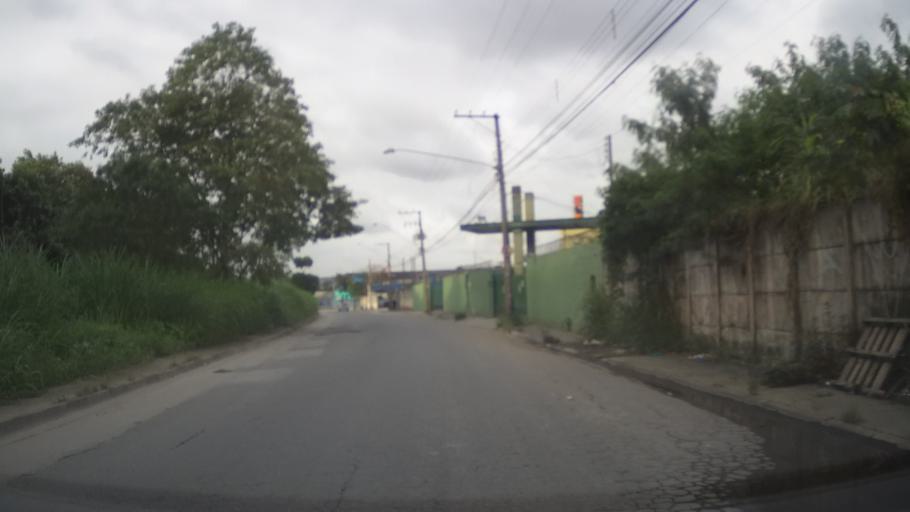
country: BR
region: Sao Paulo
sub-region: Itaquaquecetuba
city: Itaquaquecetuba
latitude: -23.4220
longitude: -46.4041
